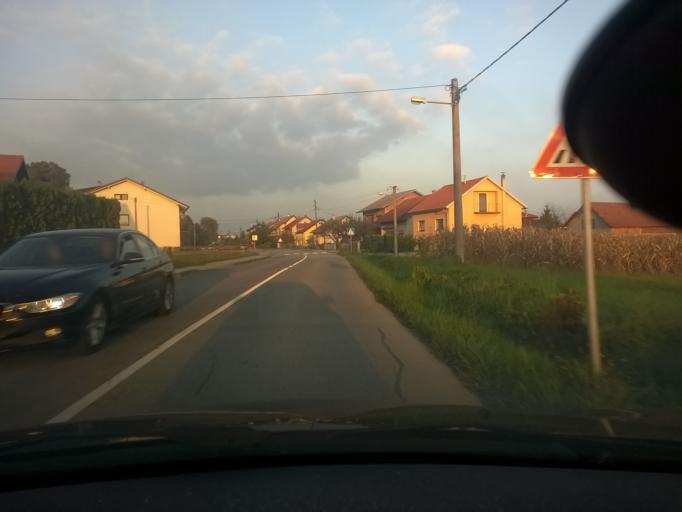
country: HR
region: Krapinsko-Zagorska
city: Zabok
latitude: 46.0157
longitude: 15.8767
